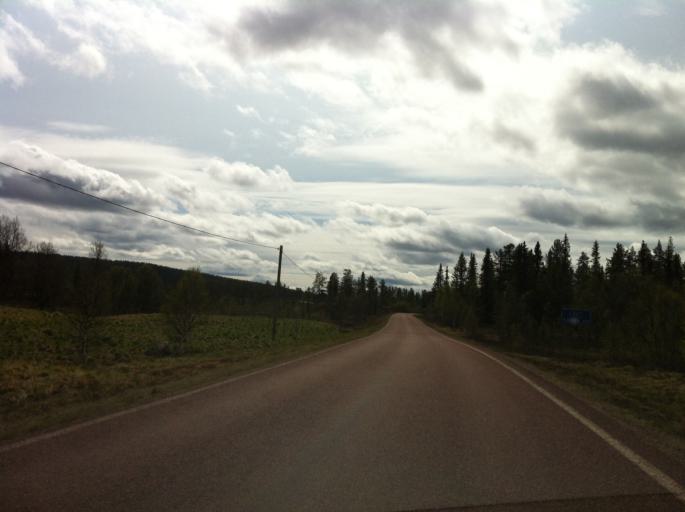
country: NO
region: Hedmark
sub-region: Engerdal
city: Engerdal
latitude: 62.1644
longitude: 12.9431
